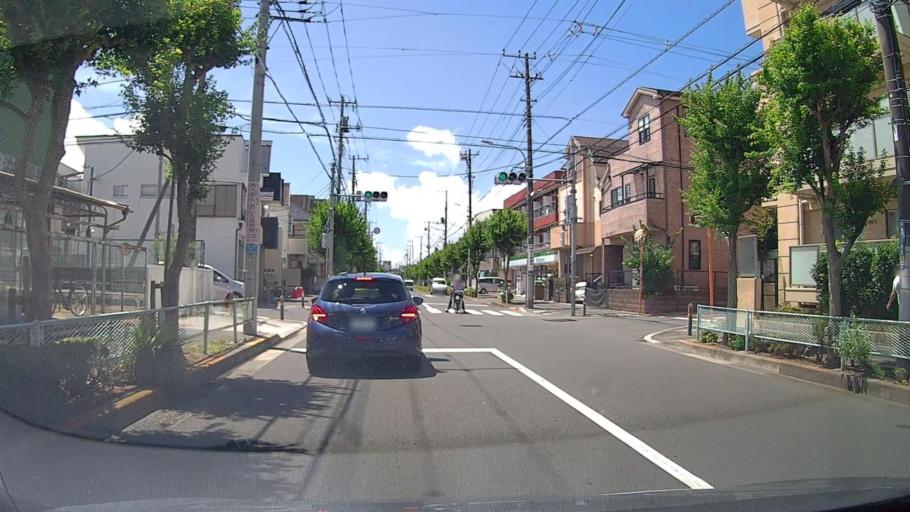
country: JP
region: Tokyo
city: Nishi-Tokyo-shi
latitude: 35.7408
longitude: 139.5659
